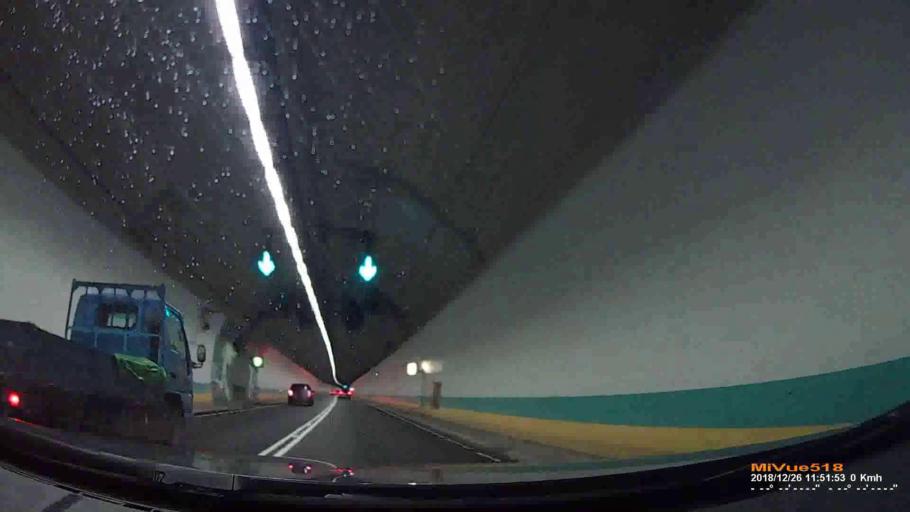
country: TW
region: Taipei
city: Taipei
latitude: 24.9712
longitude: 121.6805
